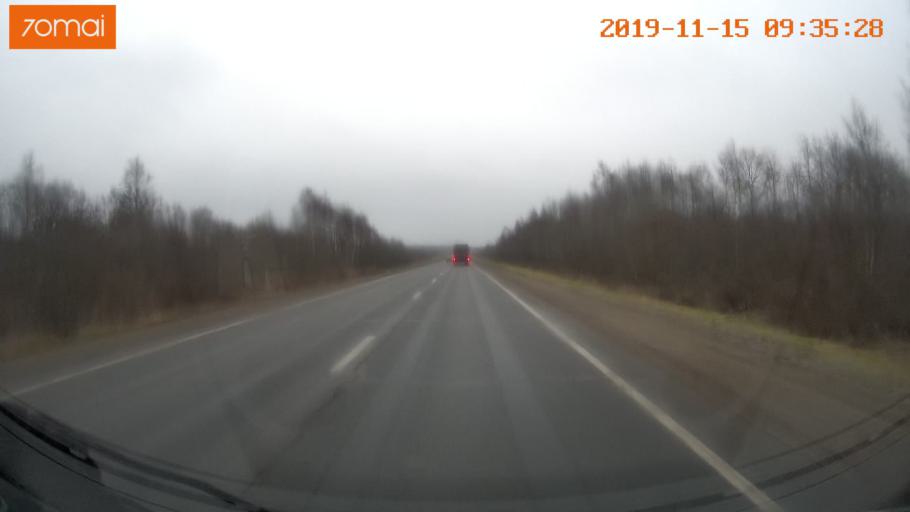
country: RU
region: Vologda
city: Sheksna
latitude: 59.2543
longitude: 38.3993
